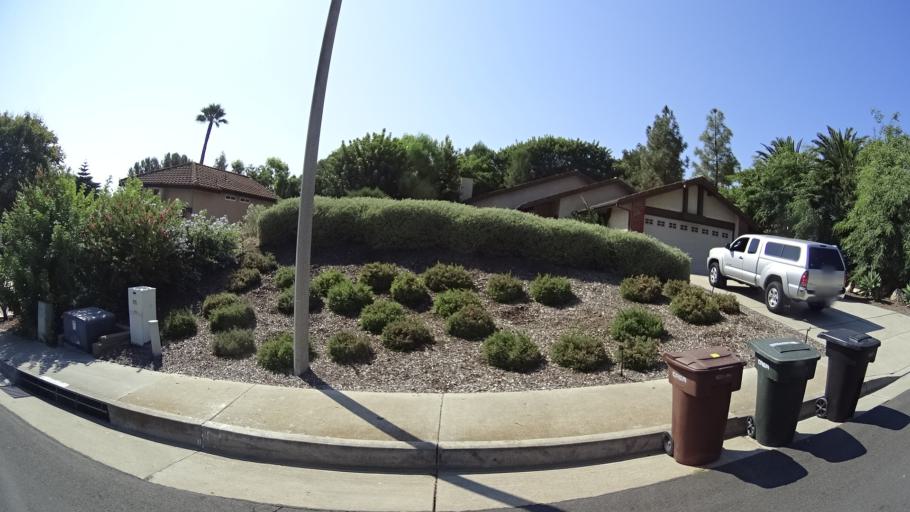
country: US
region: California
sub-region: Orange County
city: San Juan Capistrano
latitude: 33.4748
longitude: -117.6384
